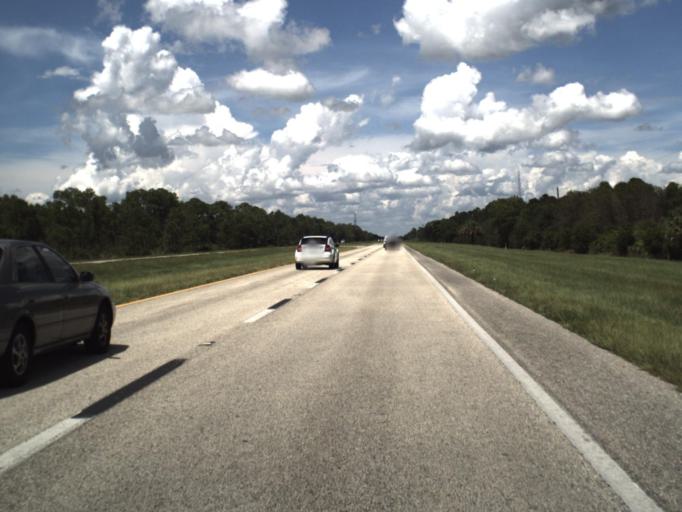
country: US
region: Florida
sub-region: Lee County
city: Burnt Store Marina
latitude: 26.8181
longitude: -81.9620
